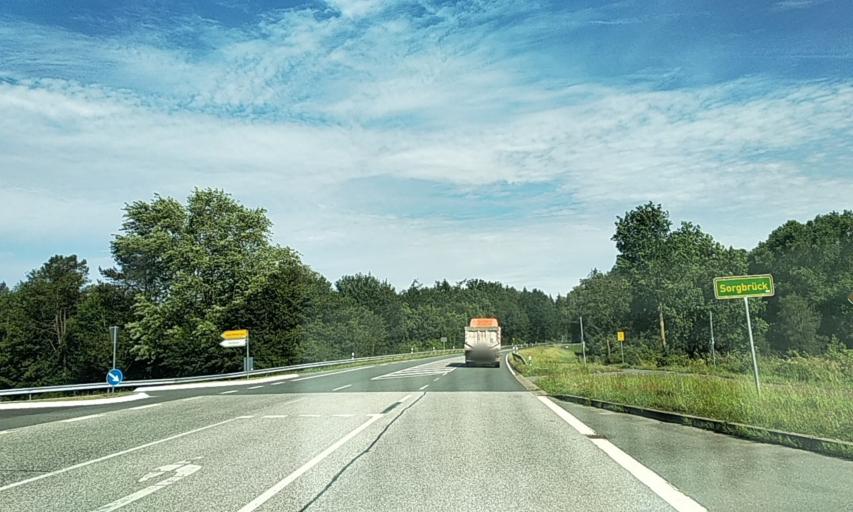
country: DE
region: Schleswig-Holstein
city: Lohe-Fohrden
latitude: 54.3558
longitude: 9.5564
